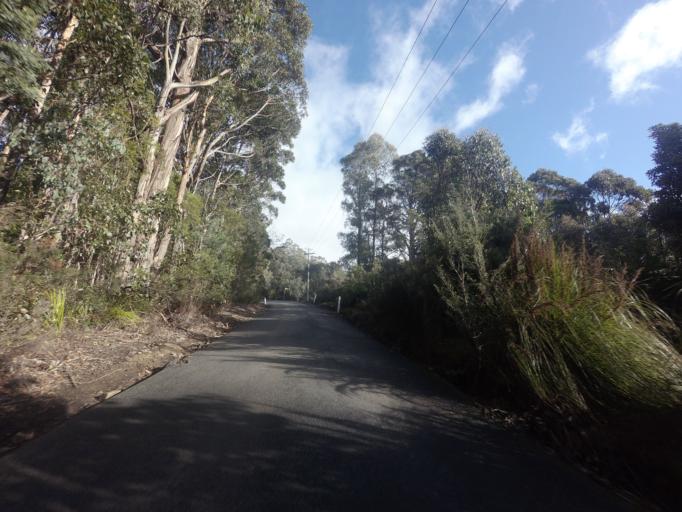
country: AU
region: Tasmania
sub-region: Glenorchy
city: Berriedale
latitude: -42.8378
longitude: 147.1591
